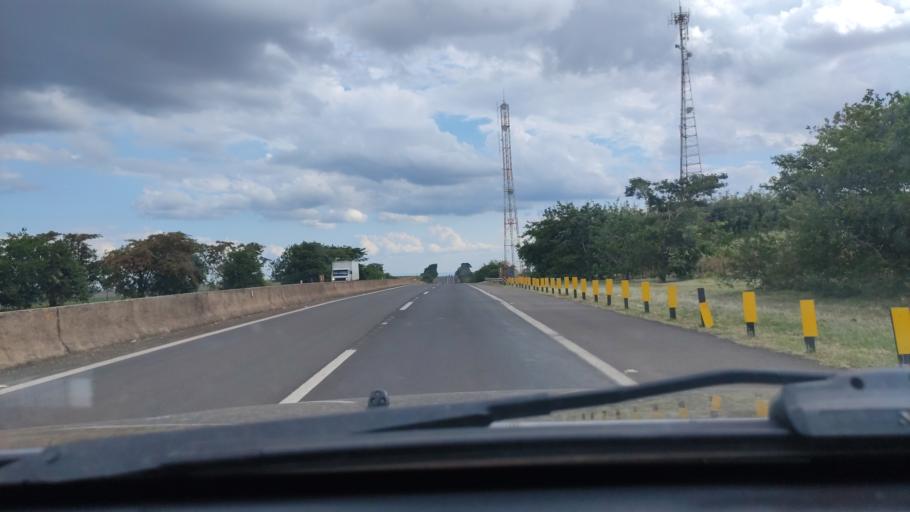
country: BR
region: Sao Paulo
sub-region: Santa Cruz Do Rio Pardo
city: Santa Cruz do Rio Pardo
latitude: -22.8229
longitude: -49.5493
